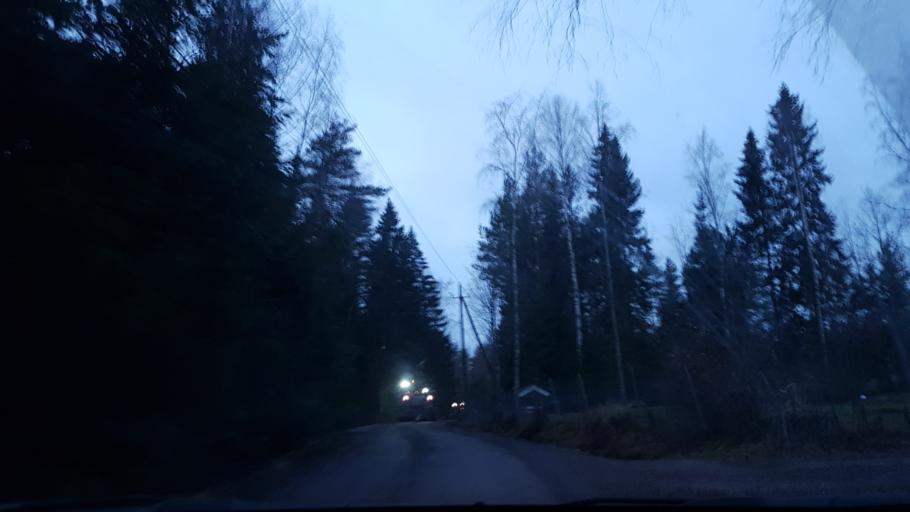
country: FI
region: Uusimaa
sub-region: Helsinki
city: Sibbo
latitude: 60.2860
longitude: 25.1770
